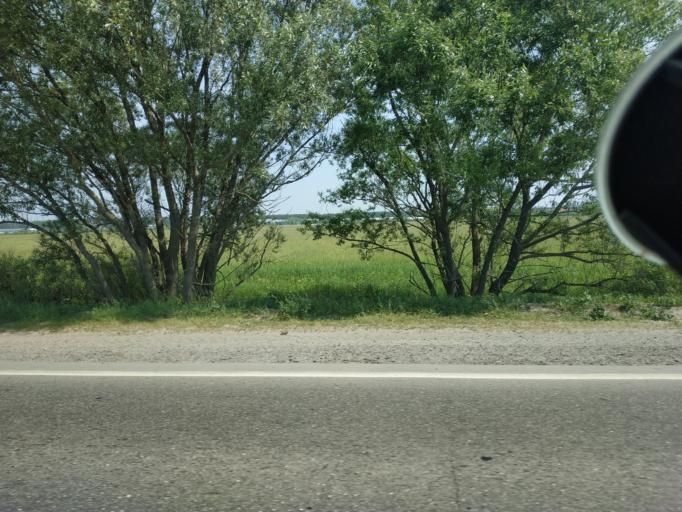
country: RU
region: Moskovskaya
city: Malyshevo
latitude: 55.5003
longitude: 38.3004
